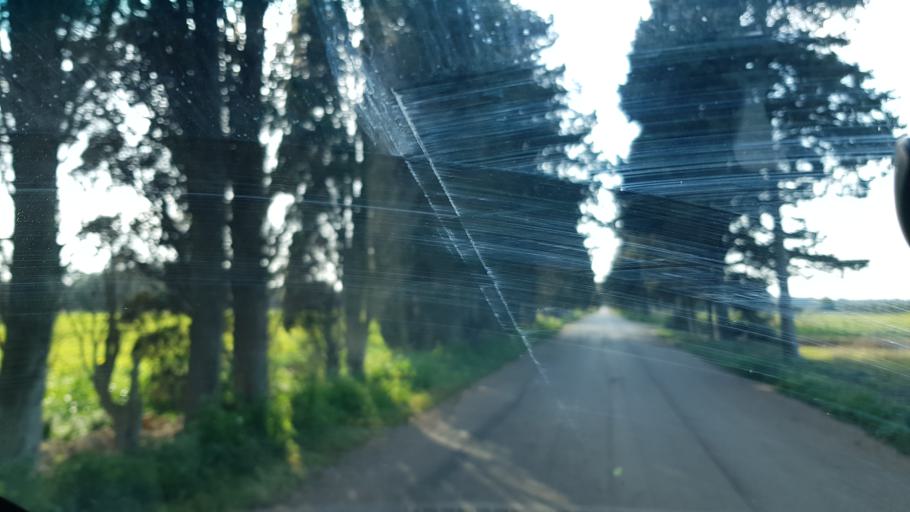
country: IT
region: Apulia
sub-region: Provincia di Brindisi
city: San Vito dei Normanni
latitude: 40.6852
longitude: 17.7853
